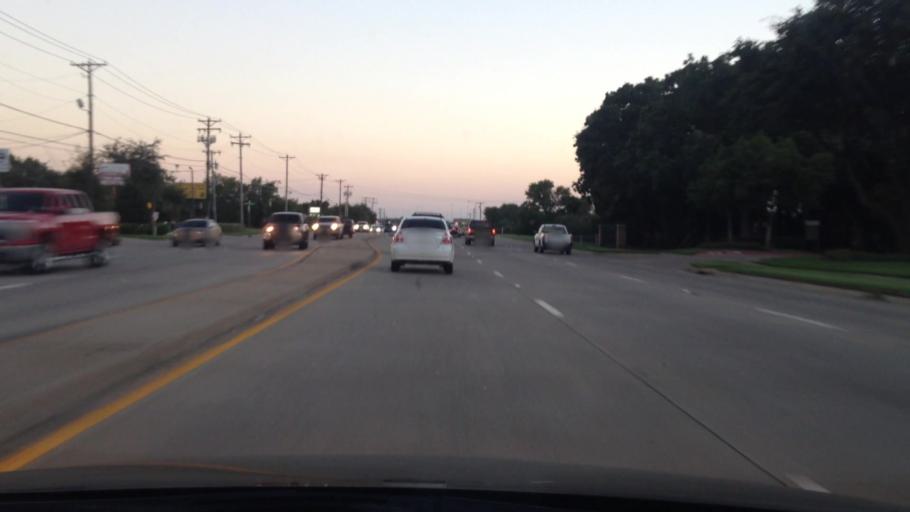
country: US
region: Texas
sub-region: Denton County
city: Lewisville
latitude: 33.0242
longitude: -96.9930
